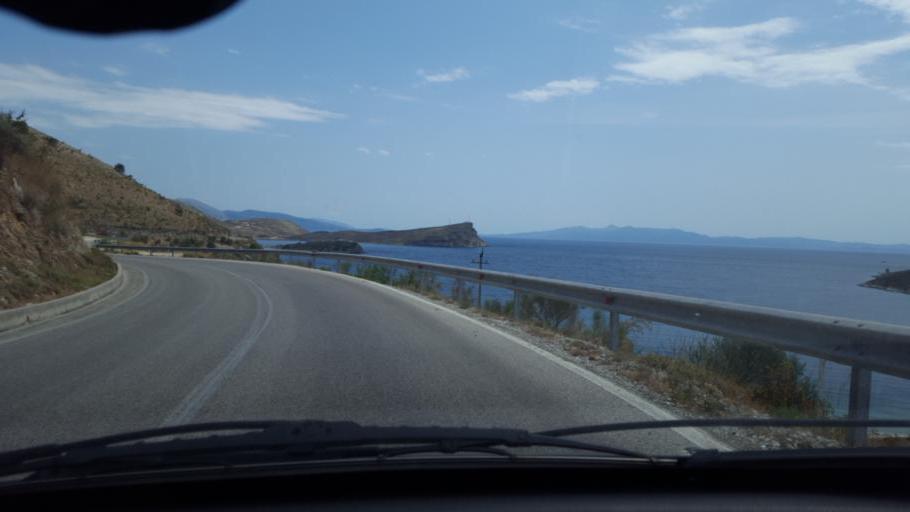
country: AL
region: Vlore
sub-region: Rrethi i Vlores
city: Himare
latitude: 40.0742
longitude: 19.7797
